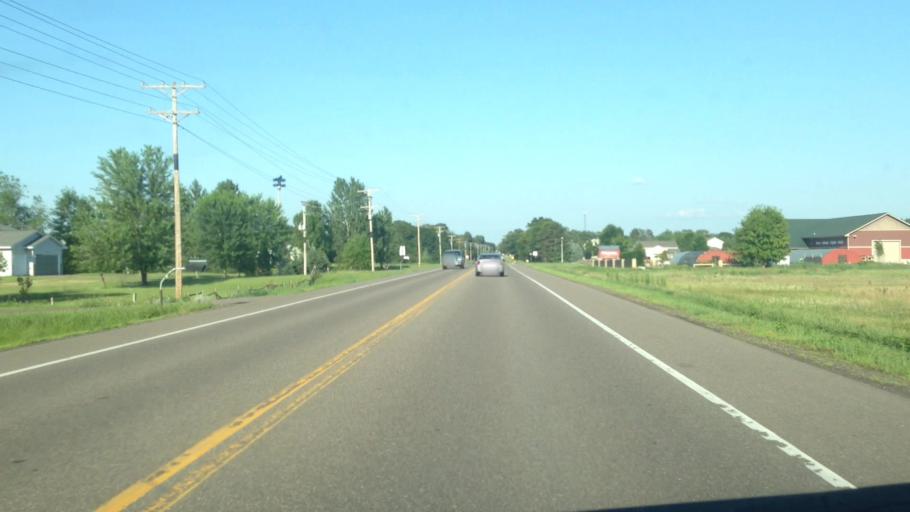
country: US
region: Minnesota
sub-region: Sherburne County
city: Zimmerman
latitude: 45.4436
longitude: -93.6109
